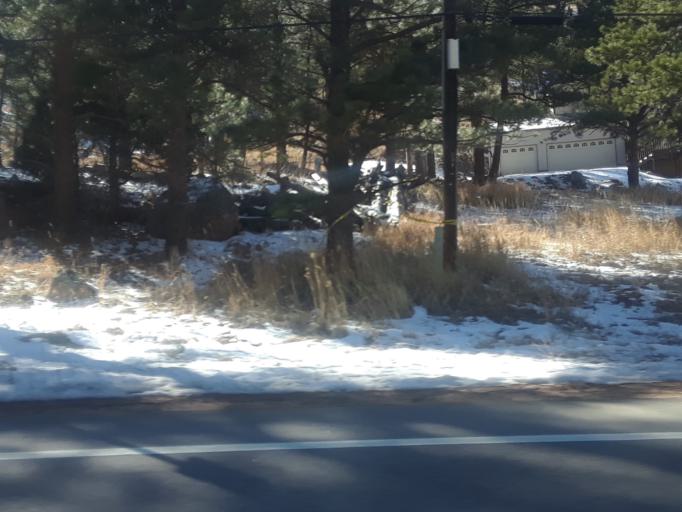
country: US
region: Colorado
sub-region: Boulder County
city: Boulder
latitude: 40.1178
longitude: -105.3068
